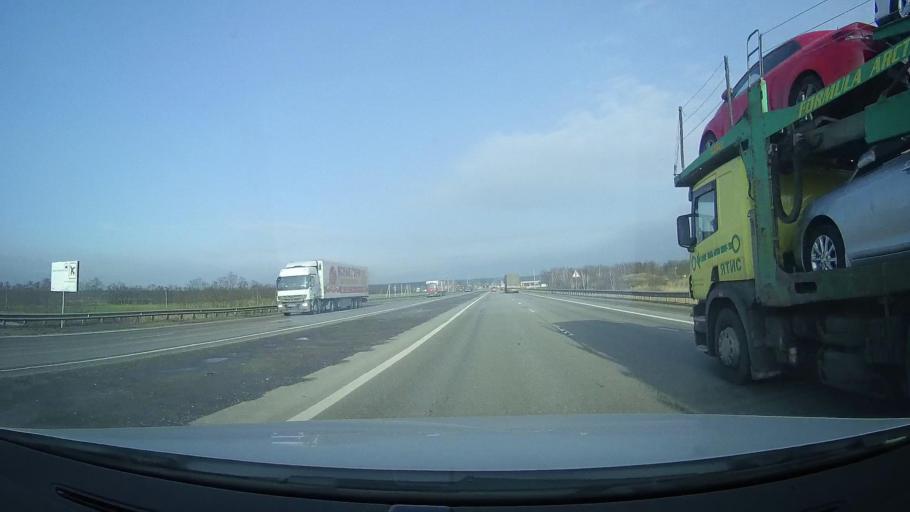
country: RU
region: Rostov
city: Grushevskaya
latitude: 47.4606
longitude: 39.9734
